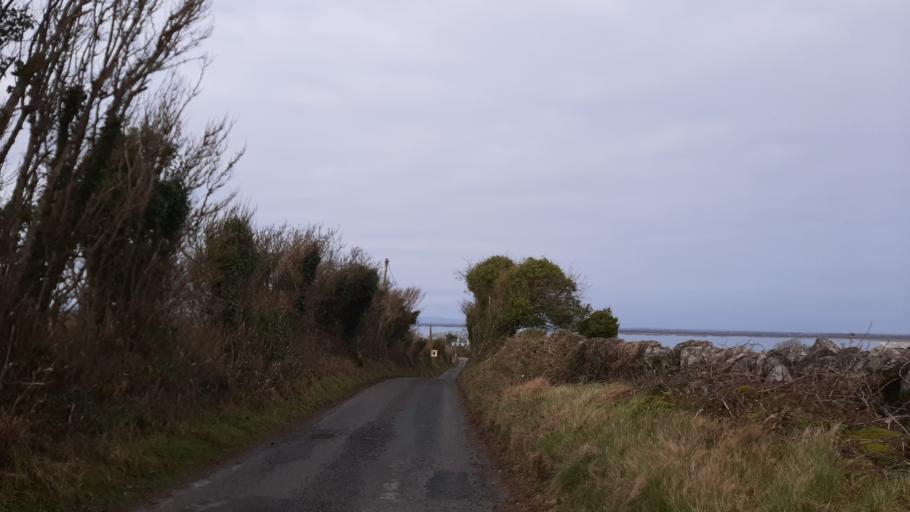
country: IE
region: Connaught
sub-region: County Galway
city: Gaillimh
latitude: 53.3160
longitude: -9.0542
